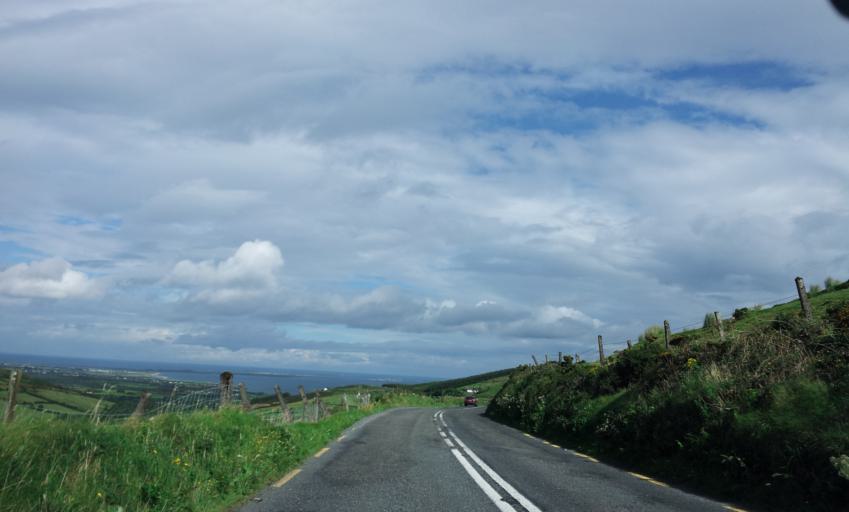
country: IE
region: Munster
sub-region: Ciarrai
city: Killorglin
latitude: 52.2022
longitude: -9.9289
